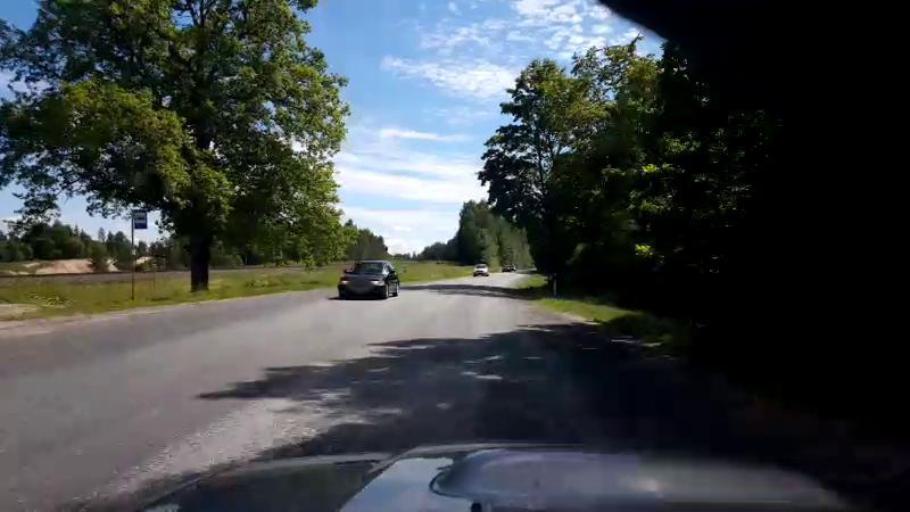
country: EE
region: Laeaene-Virumaa
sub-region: Rakke vald
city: Rakke
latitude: 58.8798
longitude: 26.2949
